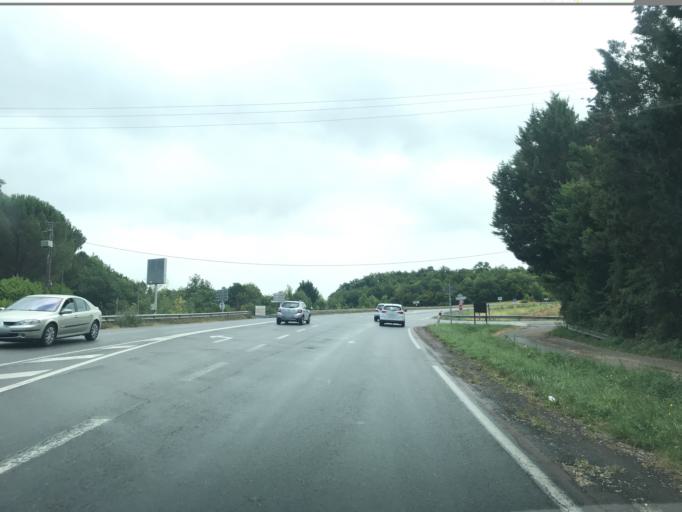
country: FR
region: Aquitaine
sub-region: Departement de la Dordogne
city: Brantome
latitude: 45.3529
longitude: 0.6560
